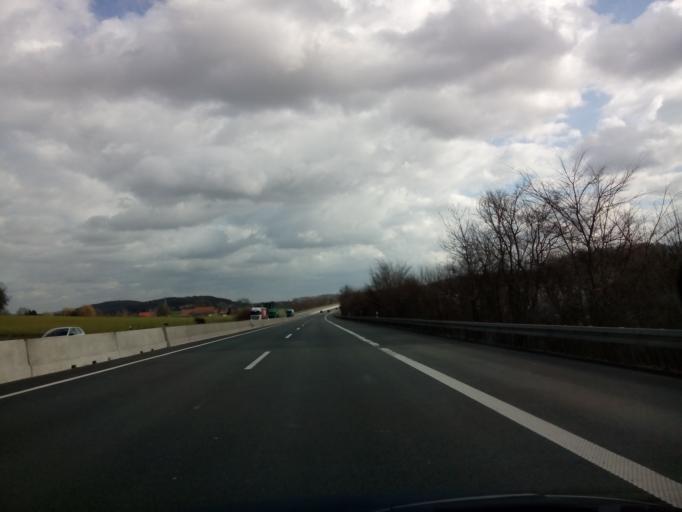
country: DE
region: Lower Saxony
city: Bissendorf
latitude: 52.2422
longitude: 8.1412
